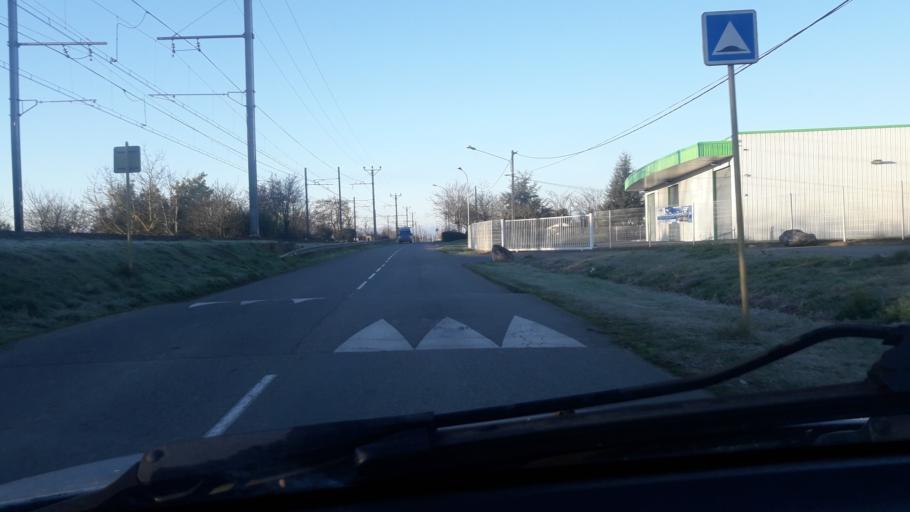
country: FR
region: Midi-Pyrenees
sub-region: Departement de la Haute-Garonne
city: Carbonne
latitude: 43.3053
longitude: 1.2207
